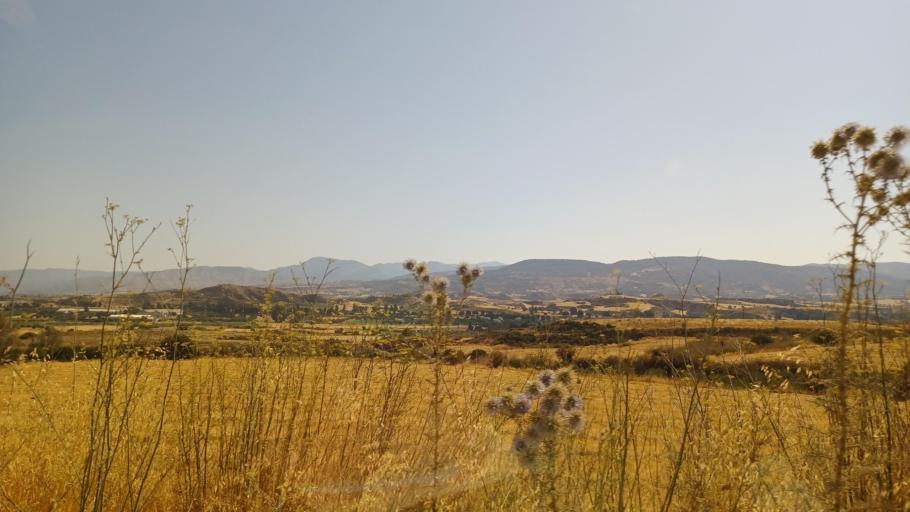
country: CY
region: Pafos
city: Polis
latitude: 35.0137
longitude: 32.4189
